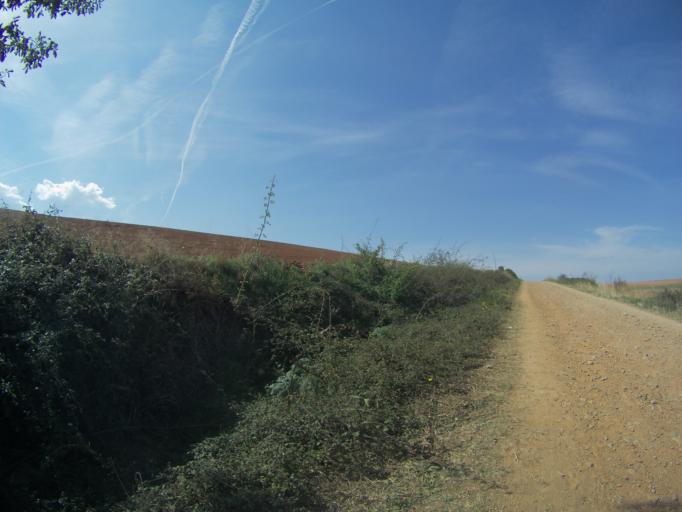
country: ES
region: La Rioja
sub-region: Provincia de La Rioja
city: Ciruena
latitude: 42.4199
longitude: -2.9140
